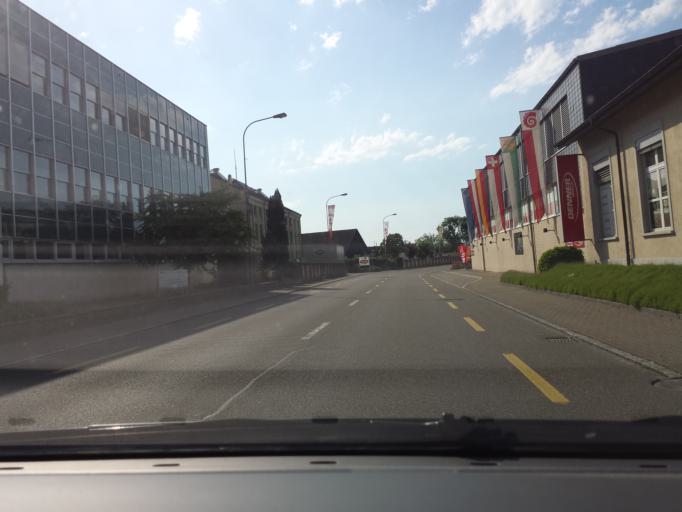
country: CH
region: Saint Gallen
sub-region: Wahlkreis Rorschach
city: Horn
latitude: 47.4980
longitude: 9.4521
